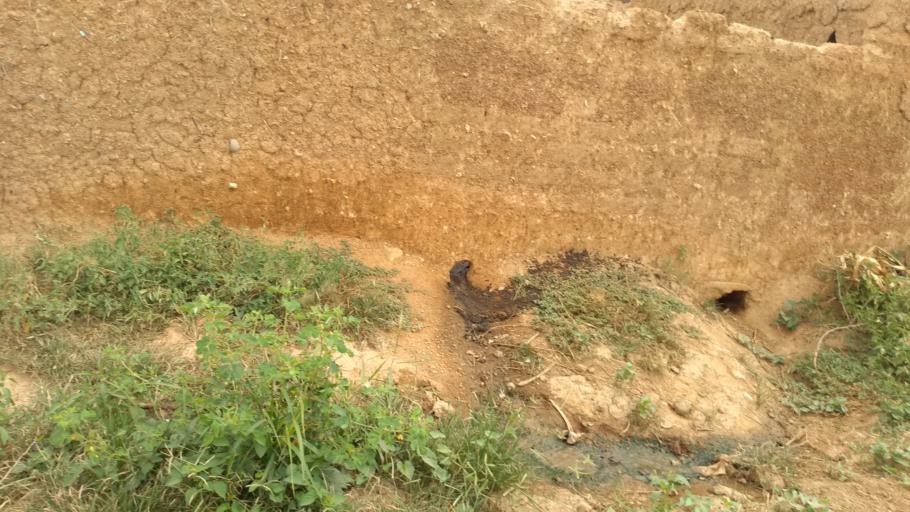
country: NG
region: Katsina
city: Kankia
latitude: 12.4379
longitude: 7.7336
